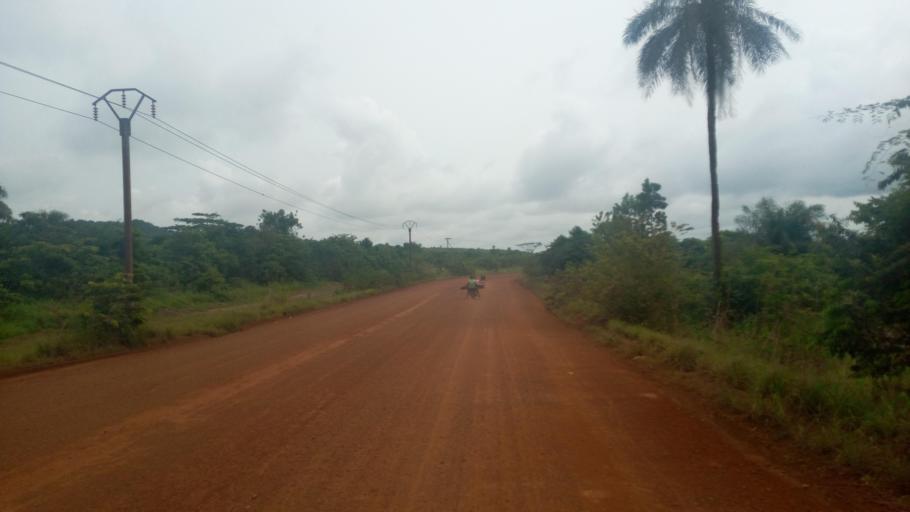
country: SL
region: Southern Province
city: Mogbwemo
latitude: 7.7193
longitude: -12.2856
